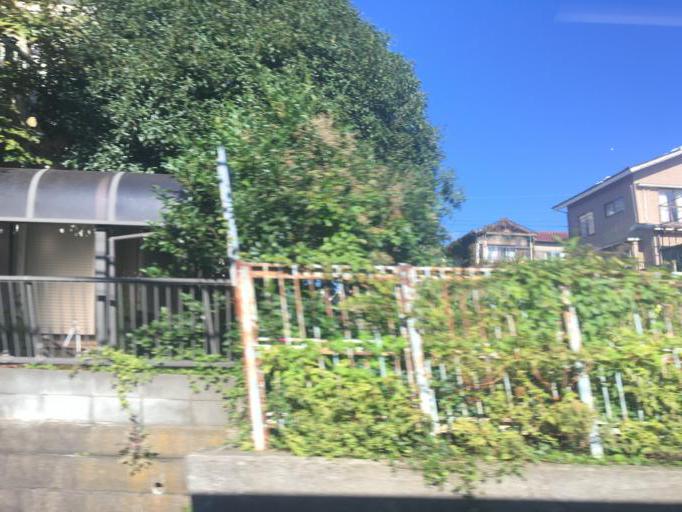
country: JP
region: Chiba
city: Yotsukaido
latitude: 35.7093
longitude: 140.1013
